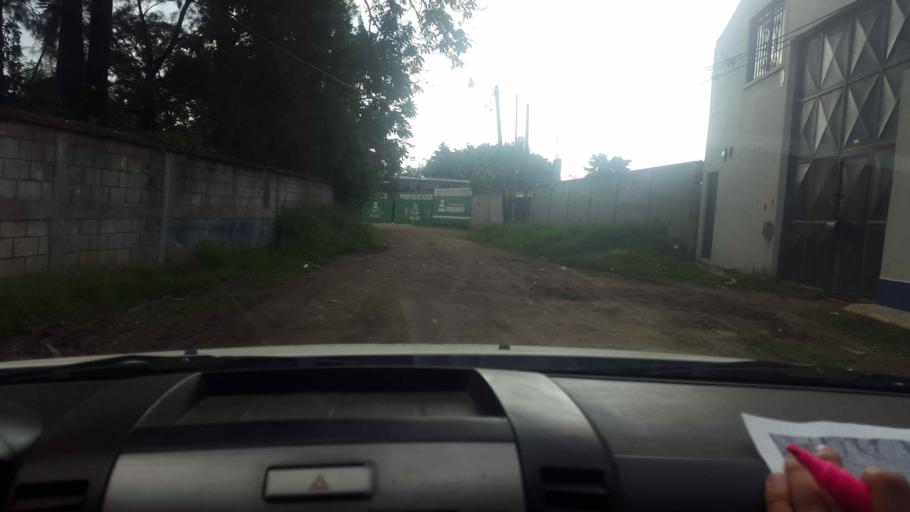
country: GT
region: Guatemala
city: Petapa
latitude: 14.5177
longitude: -90.5381
